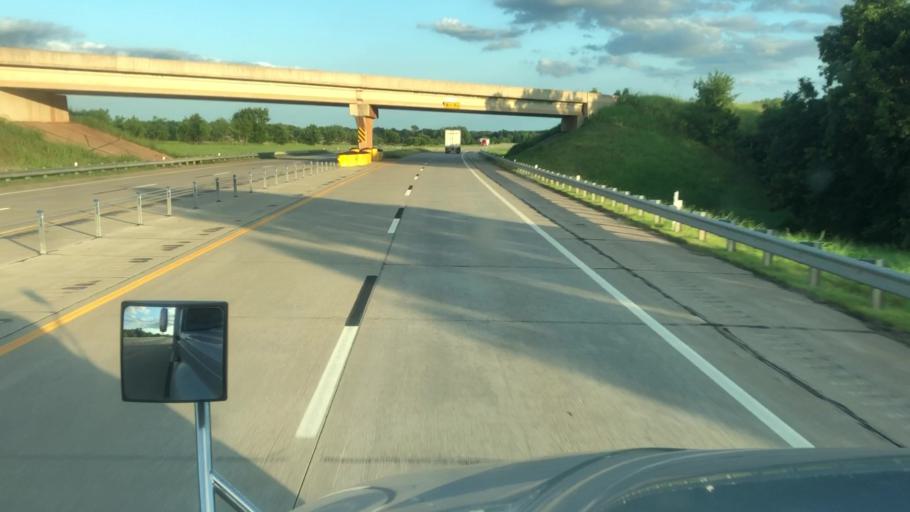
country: US
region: Oklahoma
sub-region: Pawnee County
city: Pawnee
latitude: 36.3193
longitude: -96.9973
